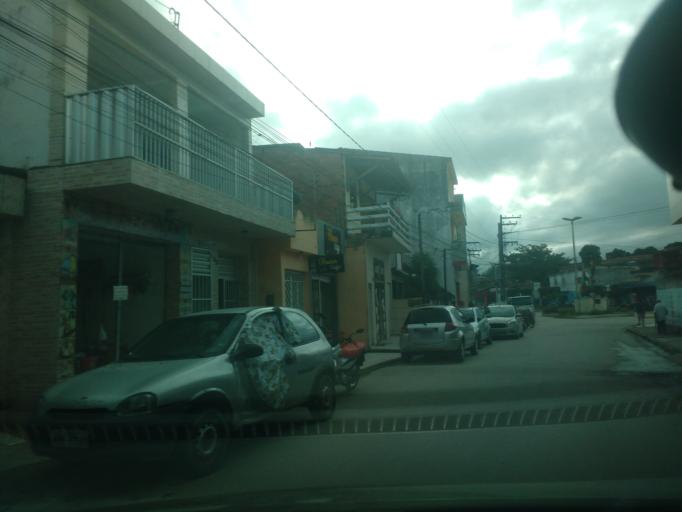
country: BR
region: Alagoas
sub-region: Uniao Dos Palmares
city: Uniao dos Palmares
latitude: -9.1569
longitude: -36.0260
